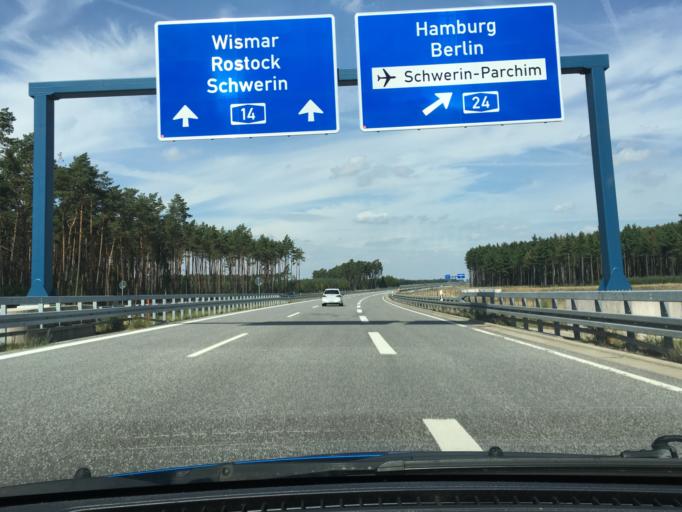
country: DE
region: Mecklenburg-Vorpommern
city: Gross Laasch
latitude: 53.4157
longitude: 11.5234
